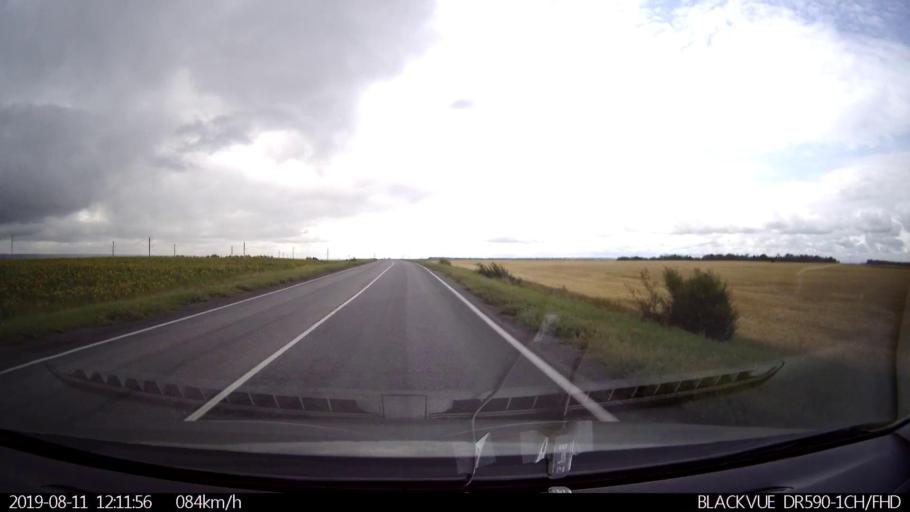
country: RU
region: Ulyanovsk
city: Silikatnyy
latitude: 53.9798
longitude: 47.9993
